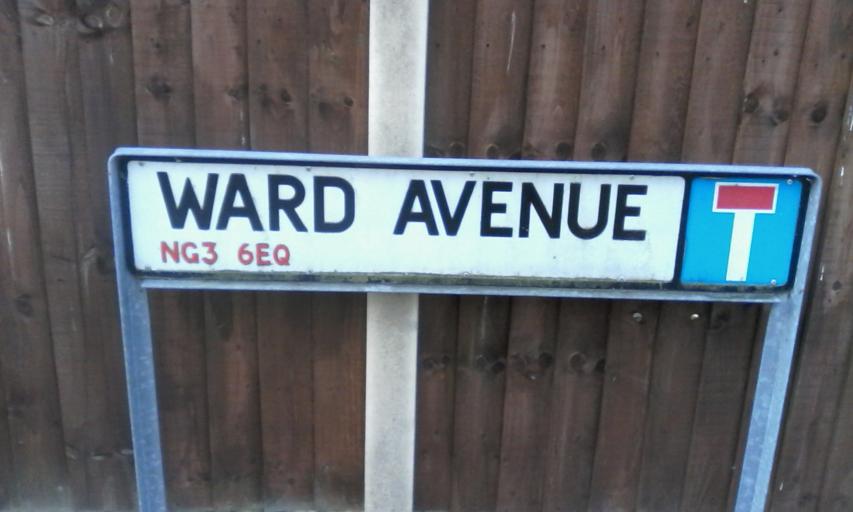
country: GB
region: England
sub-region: Nottinghamshire
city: Arnold
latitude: 52.9831
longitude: -1.1141
